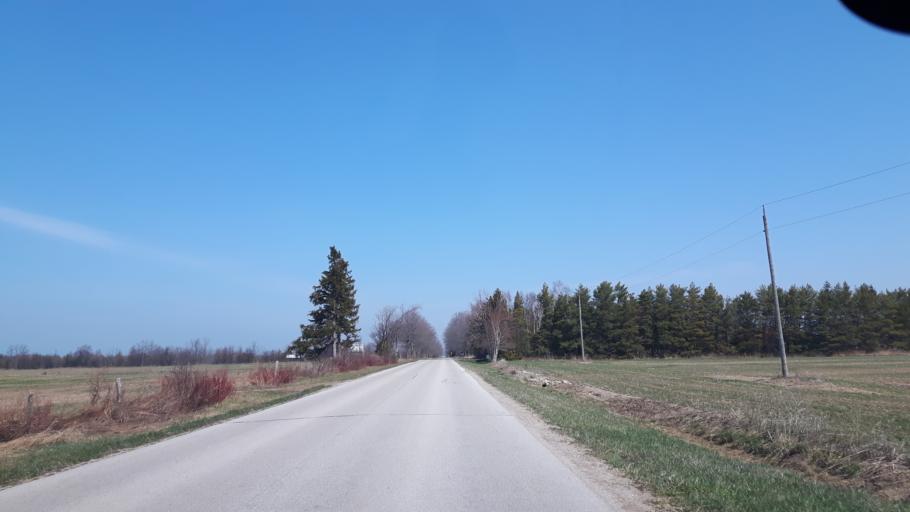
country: CA
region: Ontario
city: Goderich
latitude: 43.6507
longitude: -81.6845
